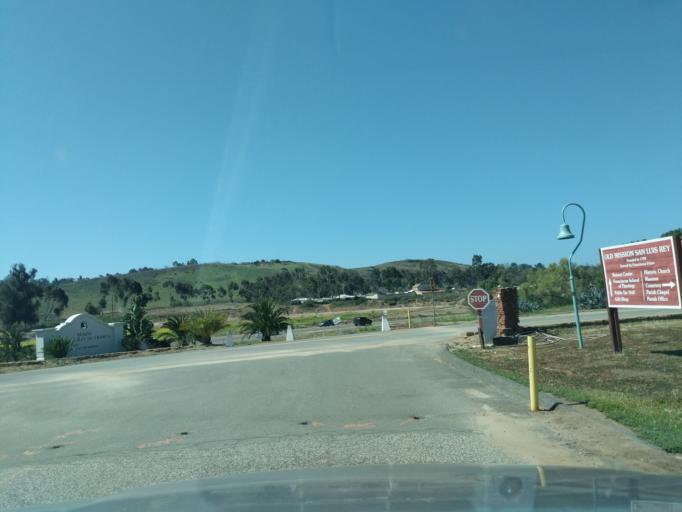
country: US
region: California
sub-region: San Diego County
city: Camp Pendleton South
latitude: 33.2311
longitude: -117.3192
